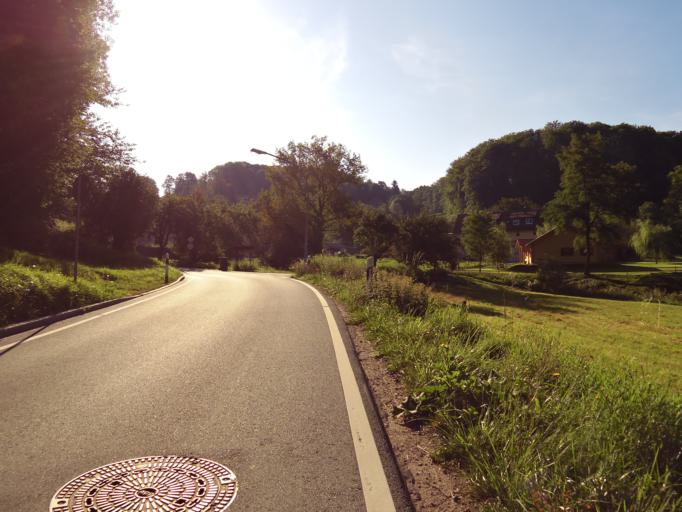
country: DE
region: Hesse
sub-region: Regierungsbezirk Darmstadt
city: Heppenheim an der Bergstrasse
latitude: 49.6665
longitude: 8.6803
